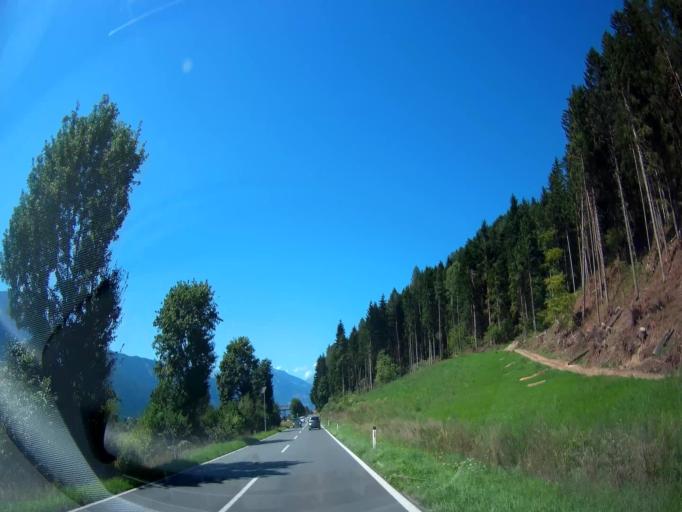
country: AT
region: Carinthia
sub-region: Politischer Bezirk Spittal an der Drau
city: Spittal an der Drau
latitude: 46.8081
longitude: 13.4785
